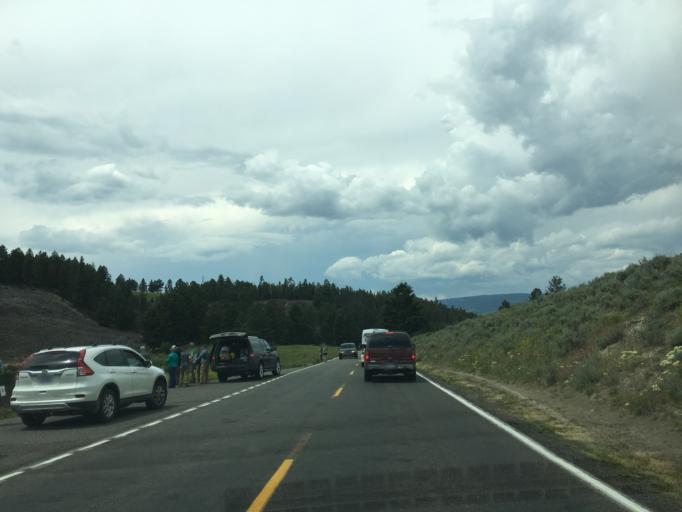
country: US
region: Montana
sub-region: Gallatin County
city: West Yellowstone
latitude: 44.9419
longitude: -110.4490
